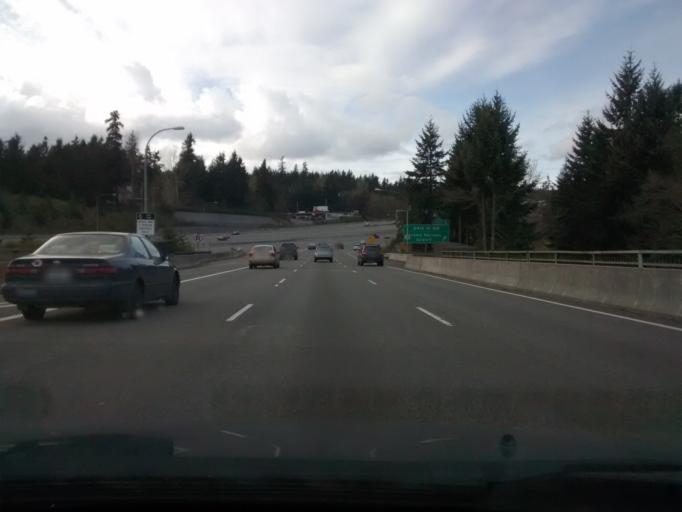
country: US
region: Washington
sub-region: Pierce County
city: Wollochet
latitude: 47.2744
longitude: -122.5579
